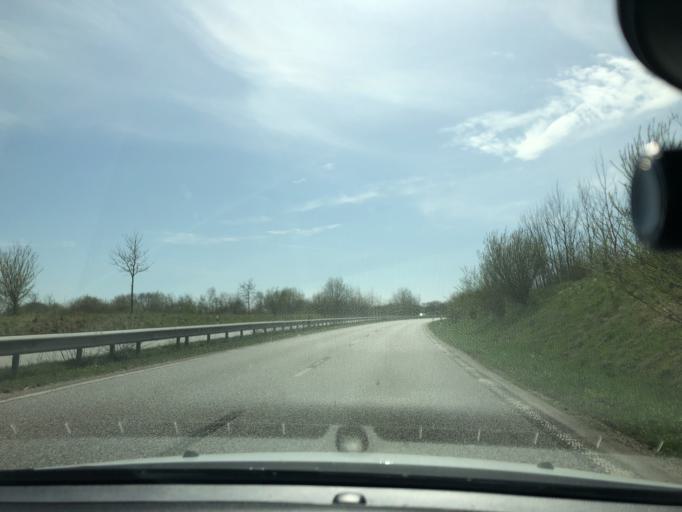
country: DE
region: Schleswig-Holstein
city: Tastrup
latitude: 54.7664
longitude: 9.4597
